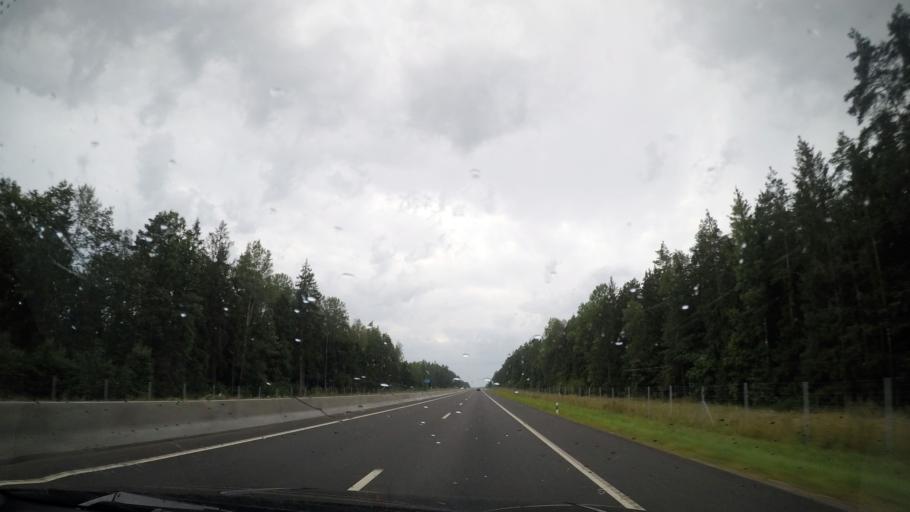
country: BY
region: Grodnenskaya
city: Lida
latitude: 53.8361
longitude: 25.1587
